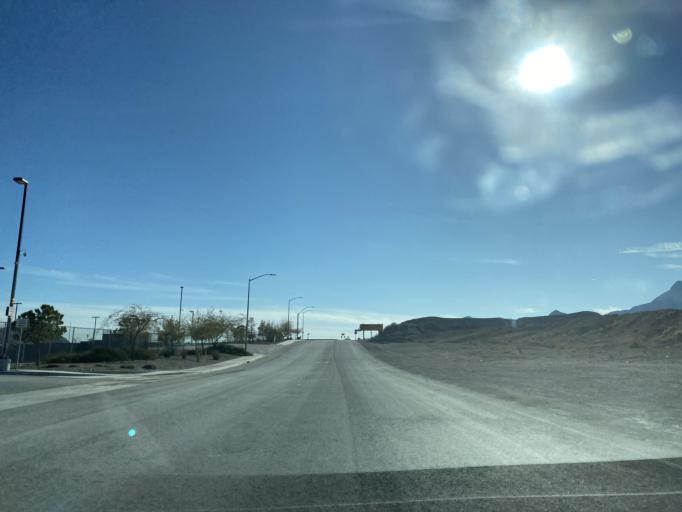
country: US
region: Nevada
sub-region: Clark County
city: Summerlin South
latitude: 36.2569
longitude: -115.3287
